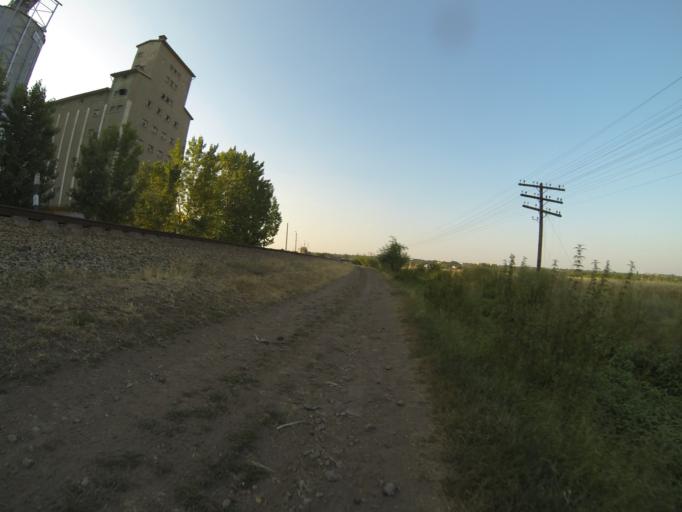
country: RO
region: Dolj
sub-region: Comuna Segarcea
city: Segarcea
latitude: 44.0849
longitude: 23.7302
